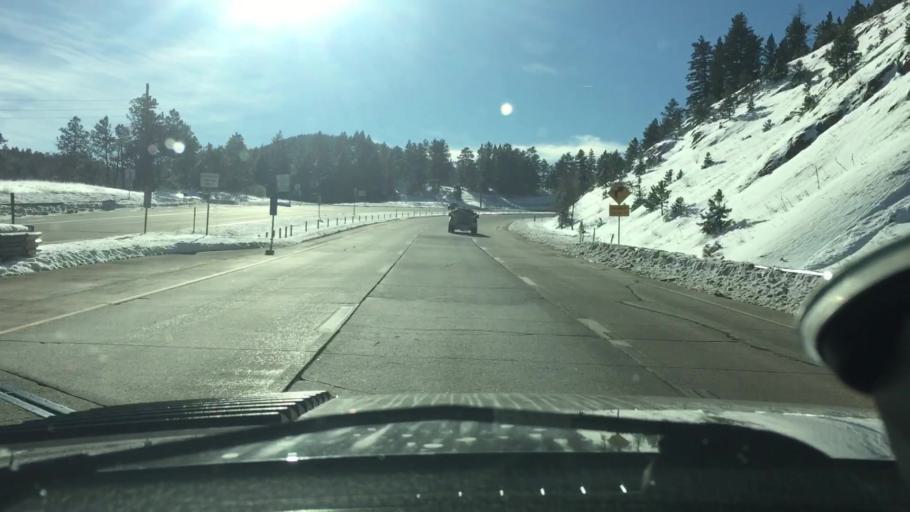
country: US
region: Colorado
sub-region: Jefferson County
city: Indian Hills
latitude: 39.5912
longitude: -105.2219
